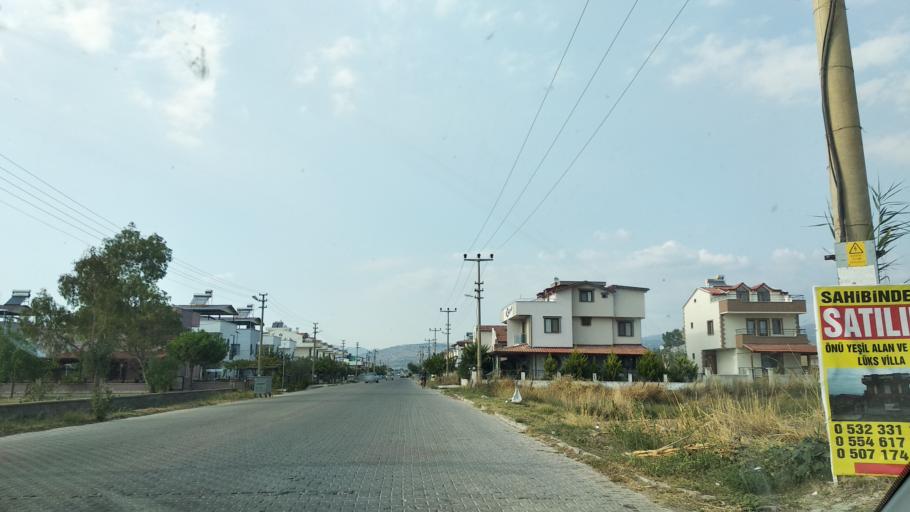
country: TR
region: Izmir
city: Dikili
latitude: 39.0999
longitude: 26.8828
